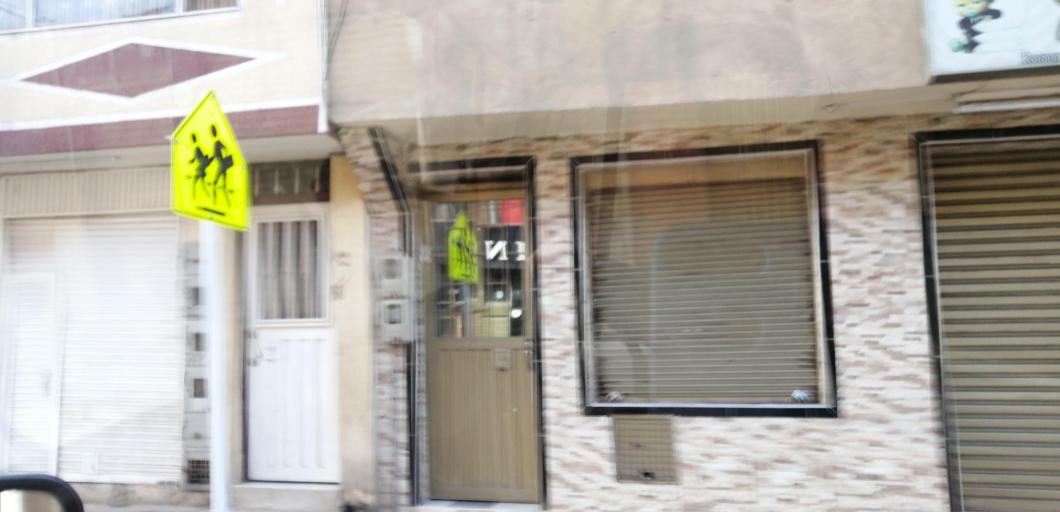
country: CO
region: Cundinamarca
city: Soacha
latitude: 4.5891
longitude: -74.1529
